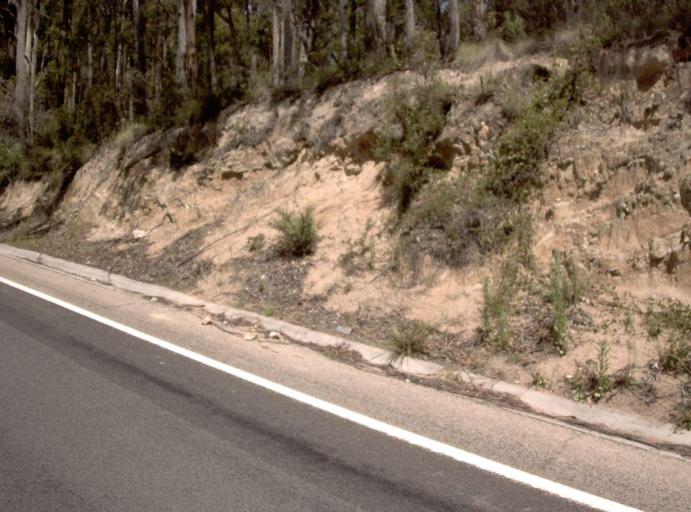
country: AU
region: New South Wales
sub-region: Bombala
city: Bombala
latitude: -37.5665
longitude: 149.3369
